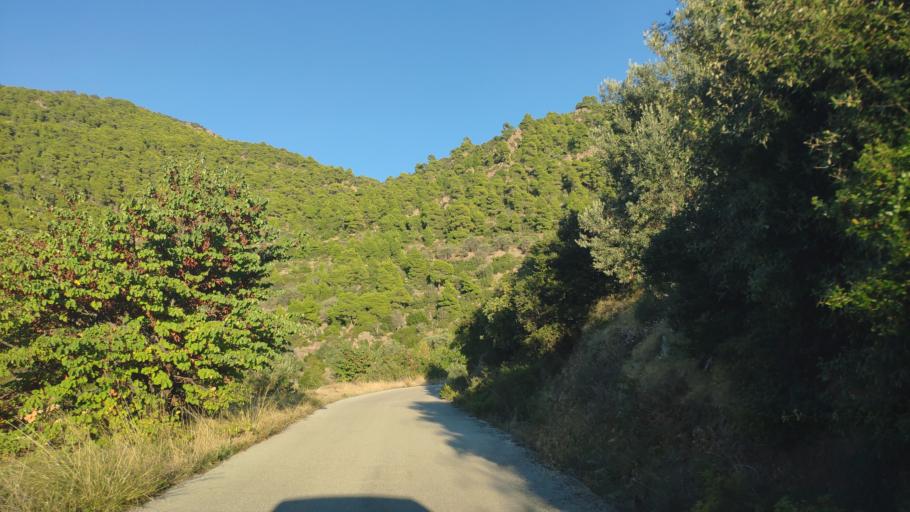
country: GR
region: Attica
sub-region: Nomos Piraios
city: Megalochori
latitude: 37.6140
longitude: 23.3352
